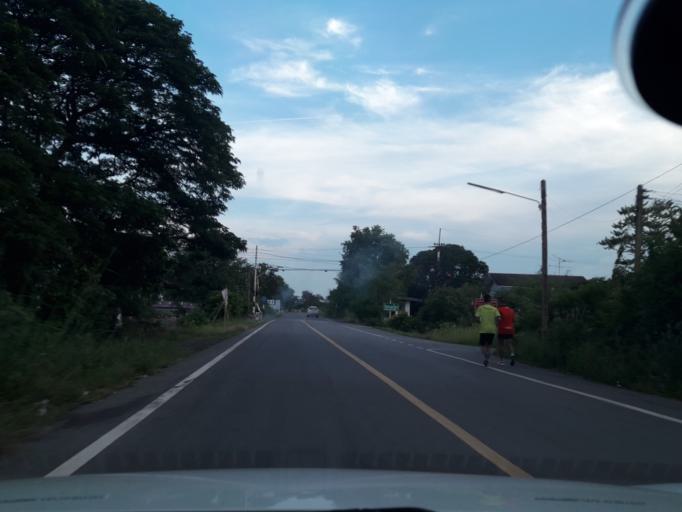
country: TH
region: Sara Buri
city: Nong Khae
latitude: 14.3071
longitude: 100.8871
